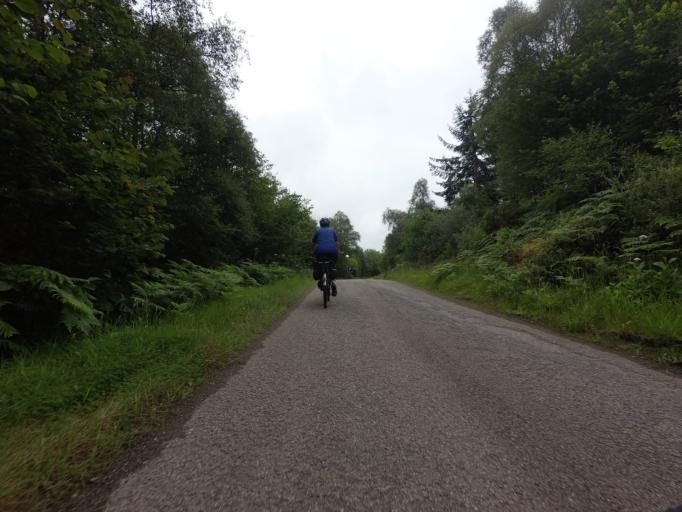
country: GB
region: Scotland
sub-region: Highland
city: Evanton
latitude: 57.9638
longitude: -4.4094
